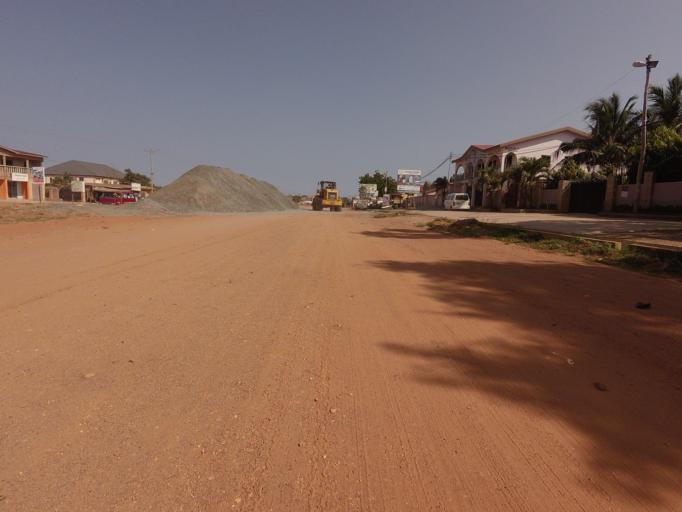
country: GH
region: Greater Accra
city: Teshi Old Town
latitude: 5.6094
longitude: -0.1232
